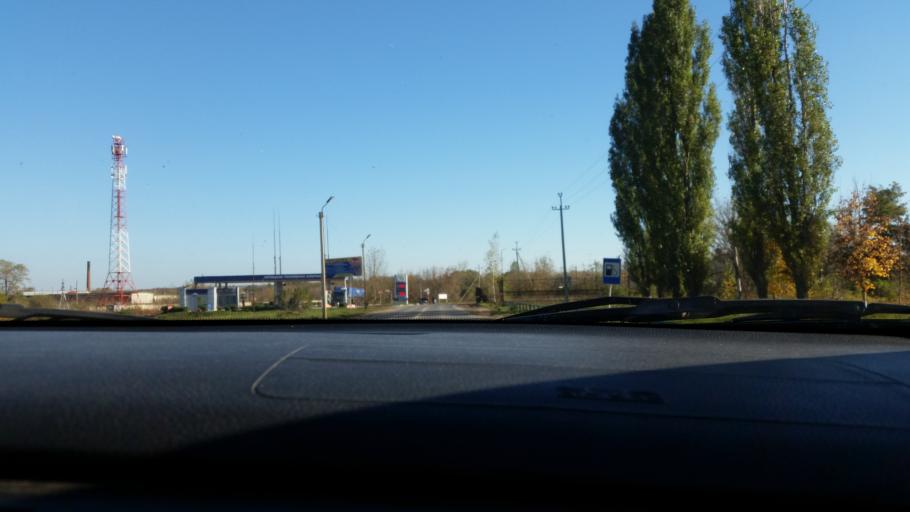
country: RU
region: Lipetsk
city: Gryazi
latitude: 52.4734
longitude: 39.9567
